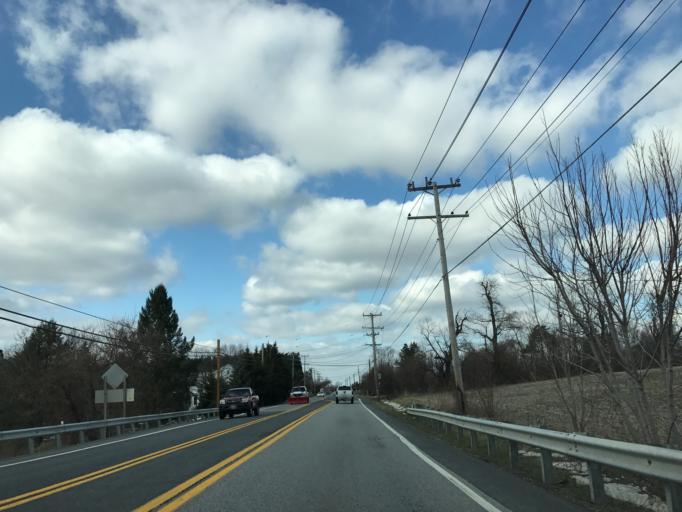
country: US
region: Maryland
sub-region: Carroll County
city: Westminster
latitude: 39.6157
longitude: -76.9972
